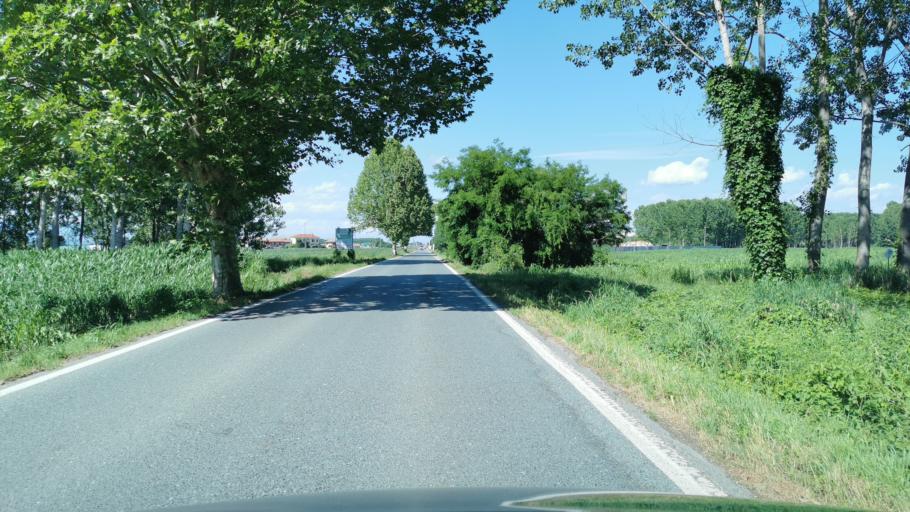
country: IT
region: Piedmont
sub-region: Provincia di Torino
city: Airasca
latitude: 44.9282
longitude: 7.4983
